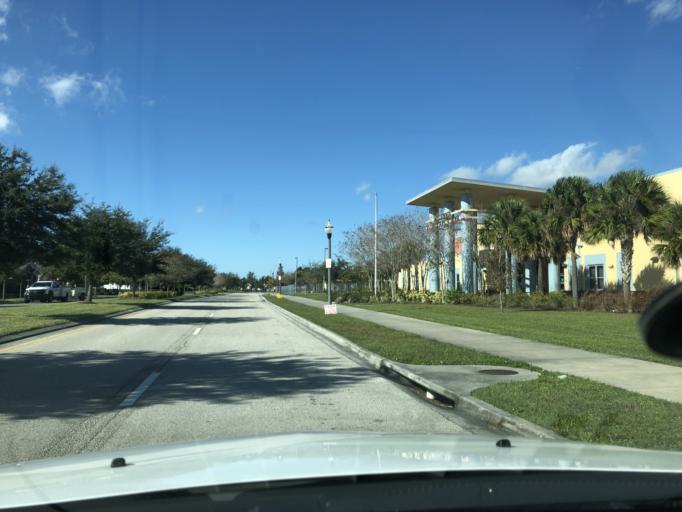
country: US
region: Florida
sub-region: Orange County
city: Oak Ridge
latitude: 28.4850
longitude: -81.4444
